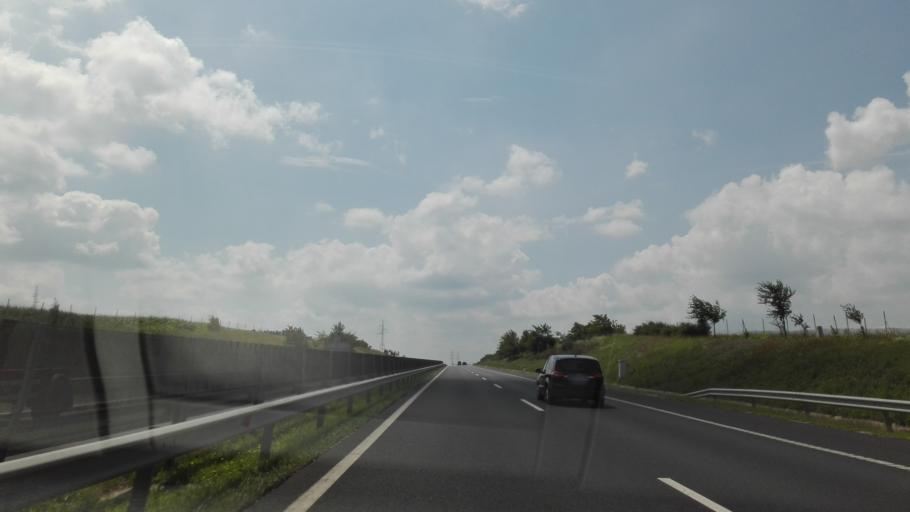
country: HU
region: Pest
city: Szazhalombatta
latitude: 47.3319
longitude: 18.8861
